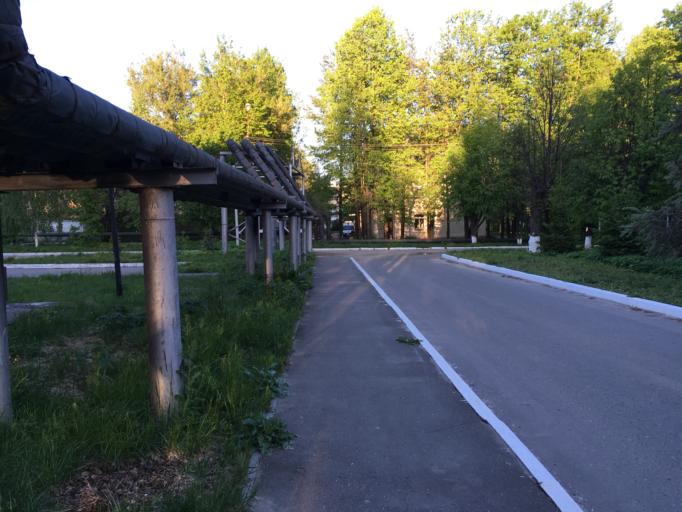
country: RU
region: Mariy-El
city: Yoshkar-Ola
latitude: 56.6502
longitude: 47.8854
